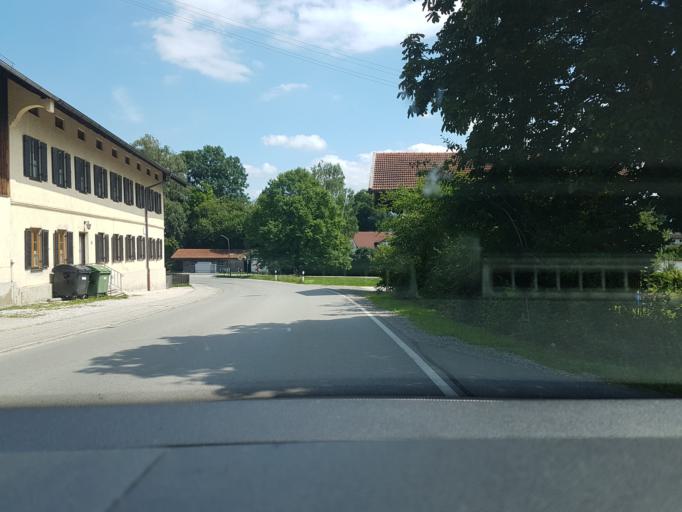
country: DE
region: Bavaria
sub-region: Upper Bavaria
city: Brannenburg
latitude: 47.7639
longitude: 12.0769
